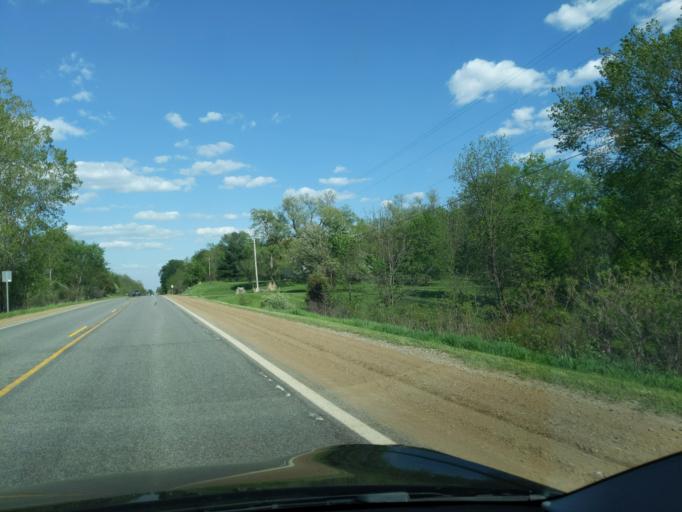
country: US
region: Michigan
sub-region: Ionia County
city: Portland
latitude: 42.7556
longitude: -84.9520
